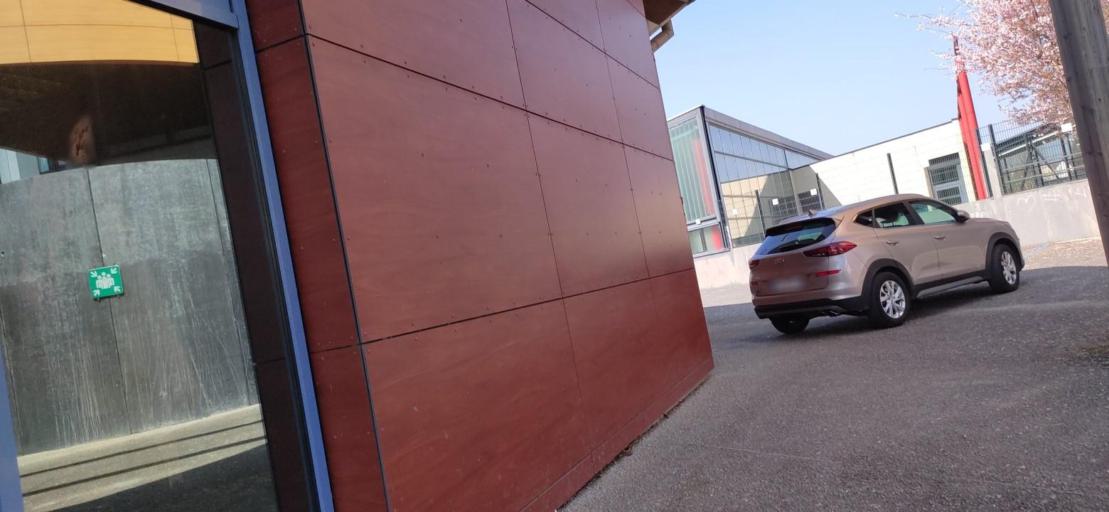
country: FR
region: Nord-Pas-de-Calais
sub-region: Departement du Pas-de-Calais
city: Aix-Noulette
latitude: 50.4372
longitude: 2.7119
